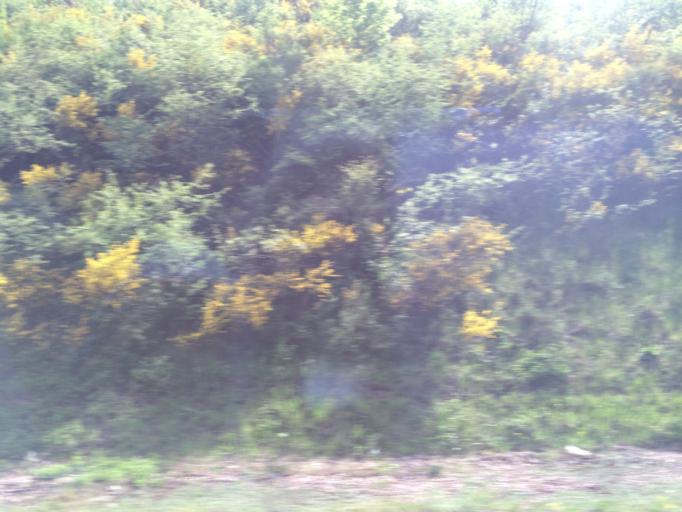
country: DE
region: Bavaria
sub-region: Regierungsbezirk Unterfranken
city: Gerbrunn
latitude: 49.7945
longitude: 9.9870
